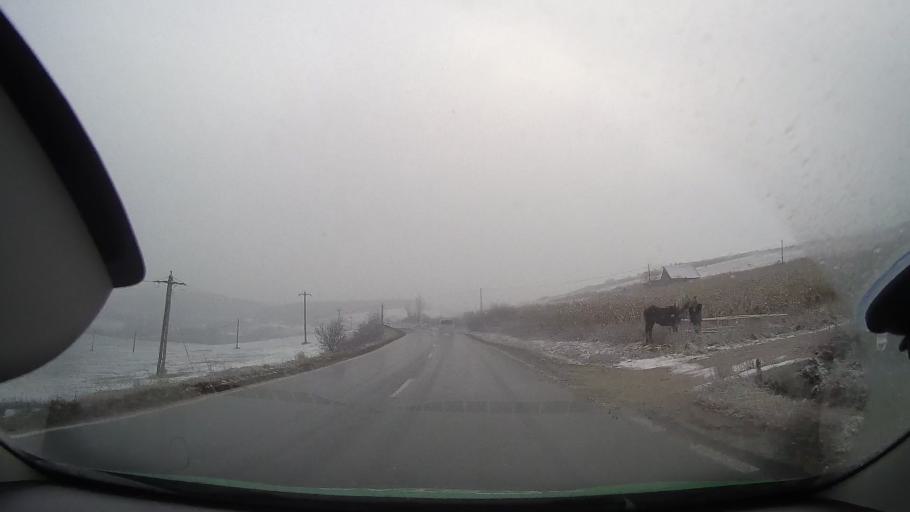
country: RO
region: Mures
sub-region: Comuna Bagaciu
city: Delenii
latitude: 46.2653
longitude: 24.3003
